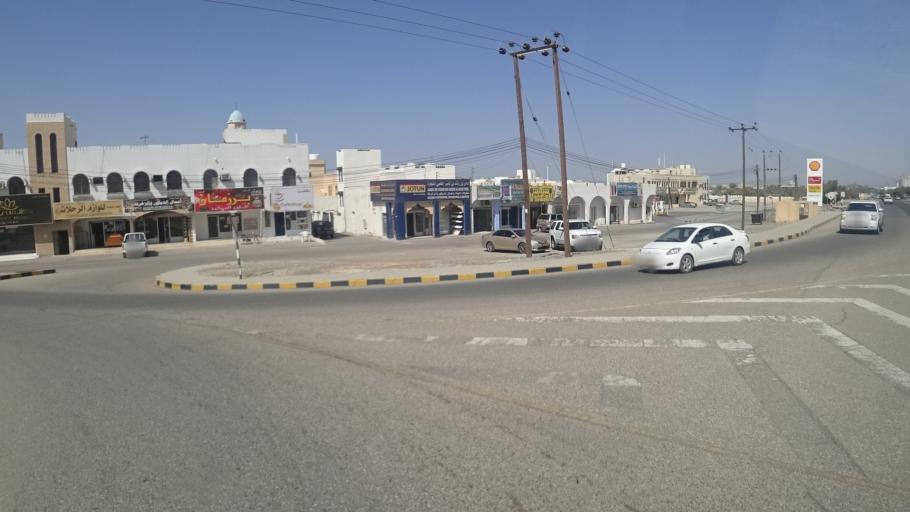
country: OM
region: Ash Sharqiyah
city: Ibra'
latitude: 22.6977
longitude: 58.5468
